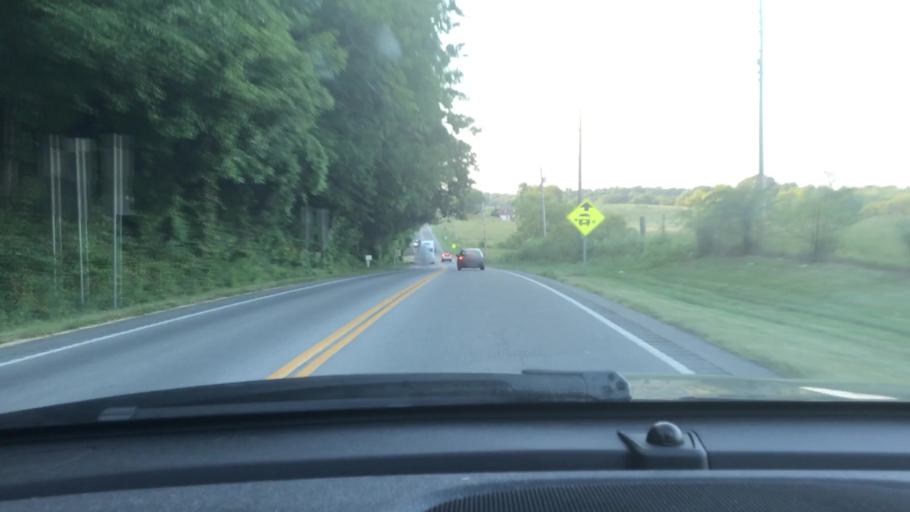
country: US
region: Tennessee
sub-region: Dickson County
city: Dickson
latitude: 36.0879
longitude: -87.3775
